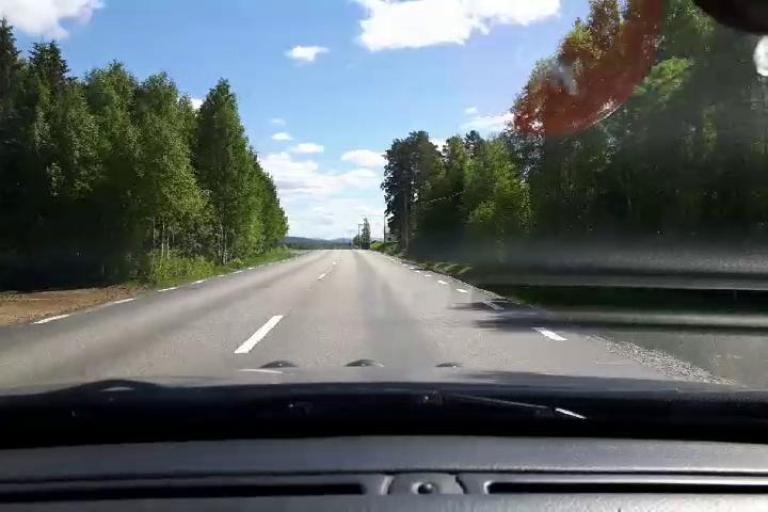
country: SE
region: Gaevleborg
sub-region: Ljusdals Kommun
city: Farila
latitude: 61.8684
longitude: 15.7300
